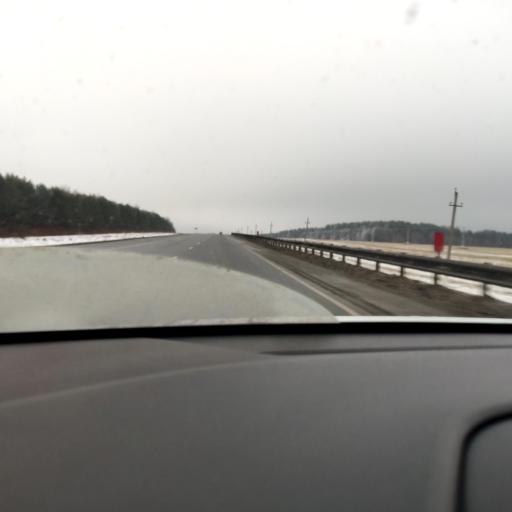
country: RU
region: Tatarstan
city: Sviyazhsk
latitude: 55.7292
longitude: 48.8103
